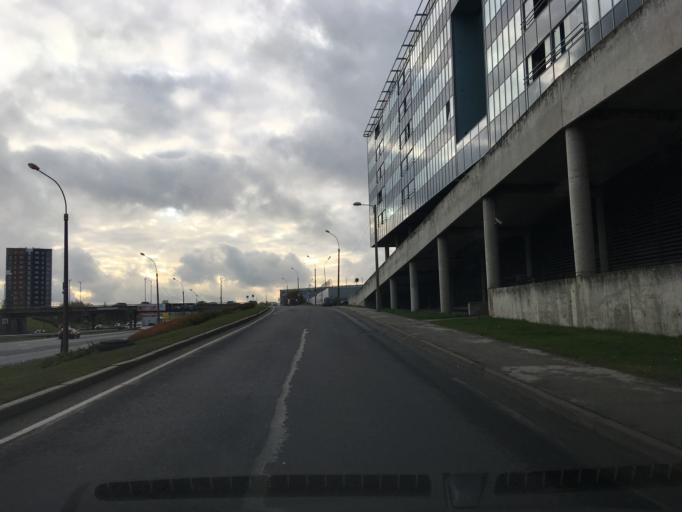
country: EE
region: Harju
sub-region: Tallinna linn
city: Tallinn
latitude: 59.4378
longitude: 24.8135
